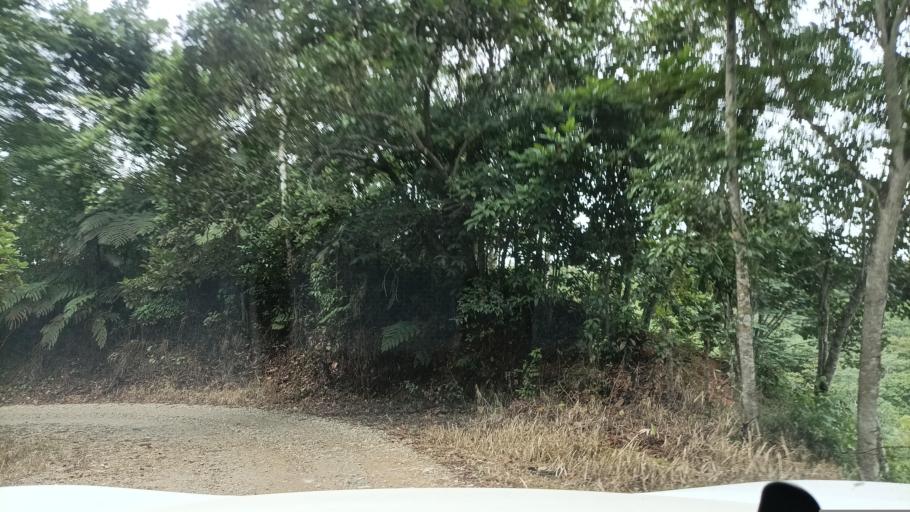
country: MX
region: Veracruz
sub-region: Uxpanapa
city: Poblado 10
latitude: 17.4420
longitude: -94.4092
